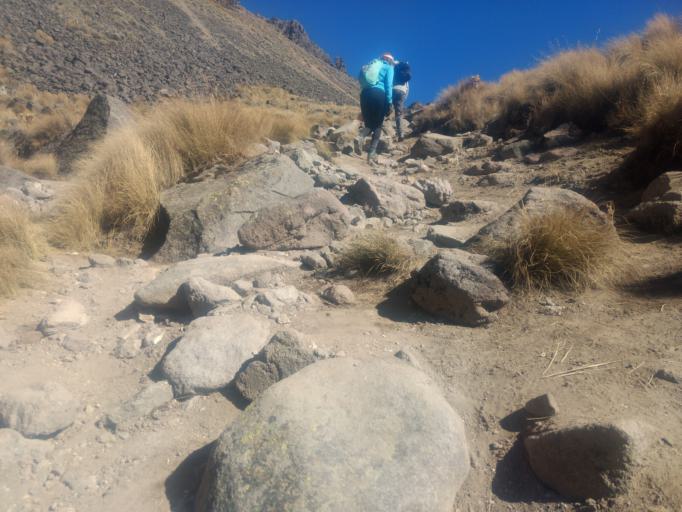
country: MX
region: Mexico
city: Cerro La Calera
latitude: 19.1129
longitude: -99.7562
